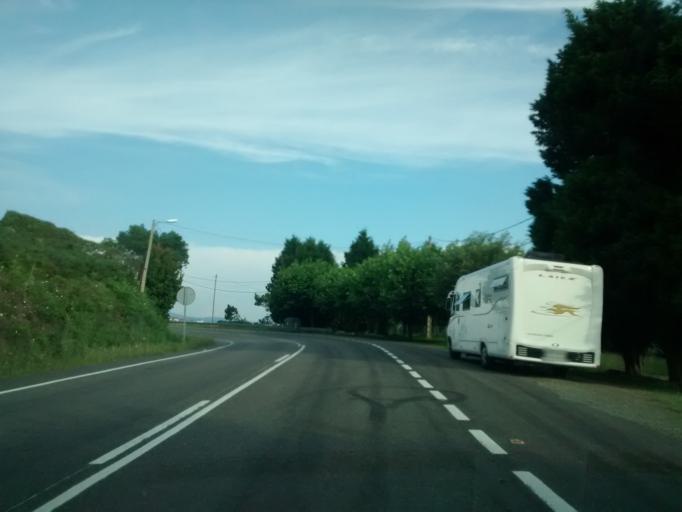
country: ES
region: Galicia
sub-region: Provincia de Pontevedra
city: Sanxenxo
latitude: 42.4127
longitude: -8.8645
